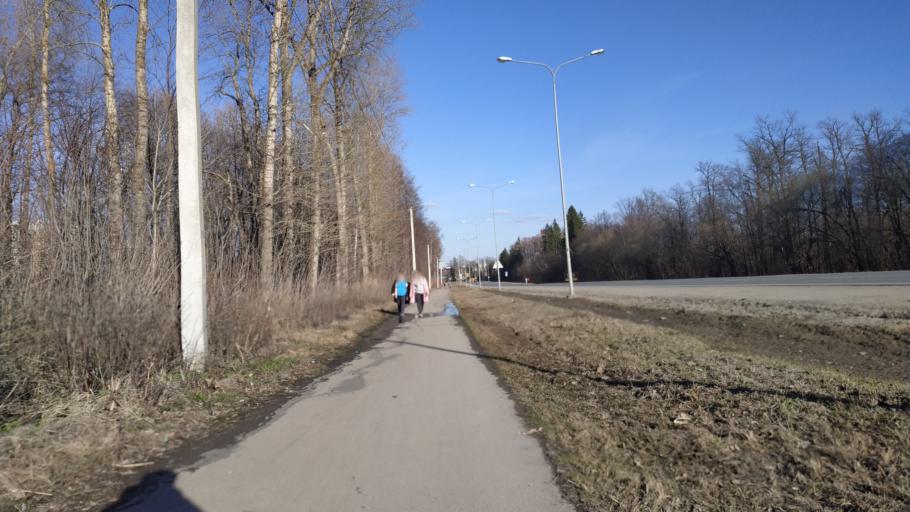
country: RU
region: Chuvashia
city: Novyye Lapsary
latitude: 56.1306
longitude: 47.1517
